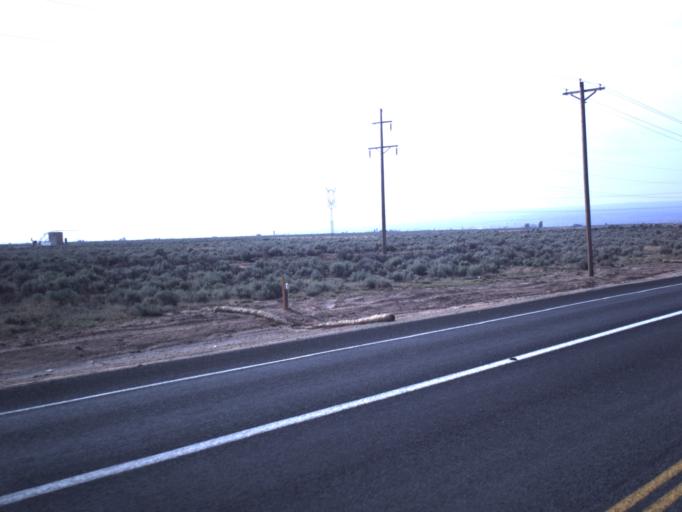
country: US
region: Utah
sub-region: Duchesne County
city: Duchesne
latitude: 40.2475
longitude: -110.3871
